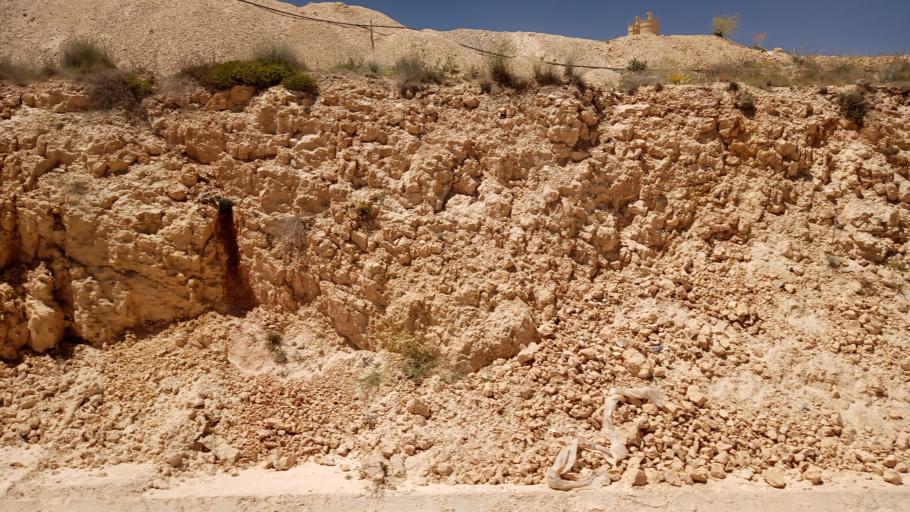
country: TR
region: Malatya
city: Darende
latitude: 38.6305
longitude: 37.4566
